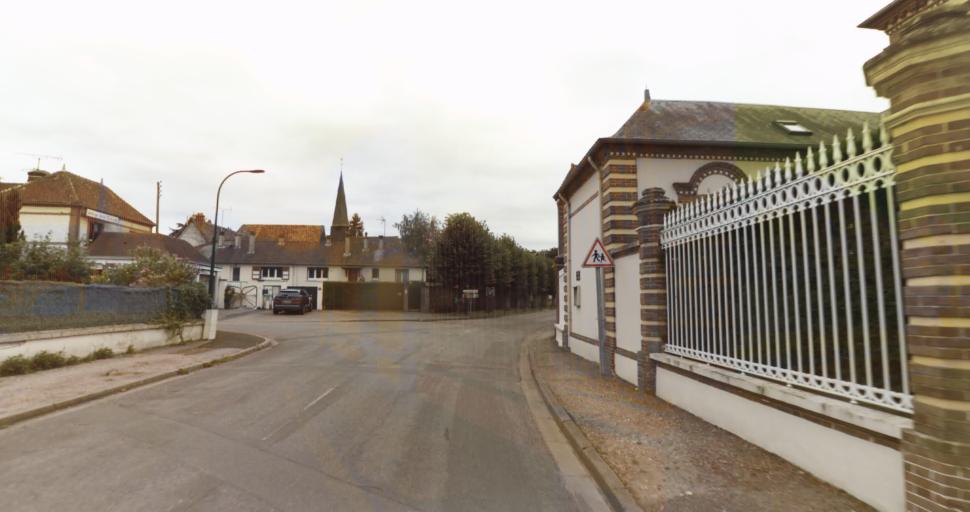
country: FR
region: Haute-Normandie
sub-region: Departement de l'Eure
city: Croth
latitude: 48.8448
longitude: 1.3787
